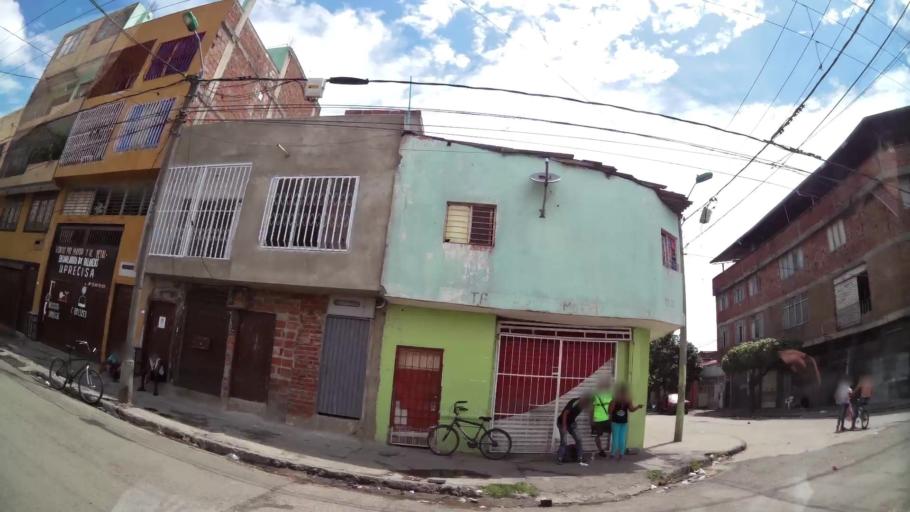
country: CO
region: Valle del Cauca
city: Cali
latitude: 3.4449
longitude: -76.5229
